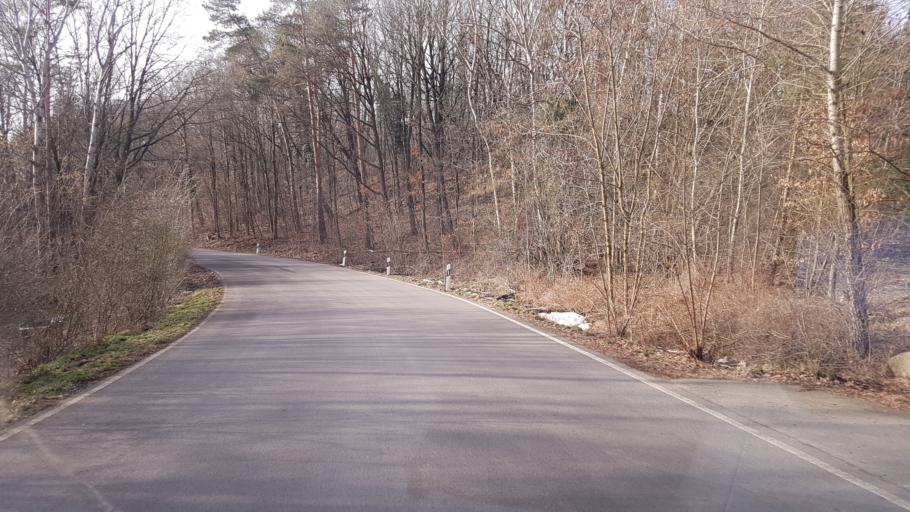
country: DE
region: Brandenburg
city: Schipkau
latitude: 51.5306
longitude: 13.8270
